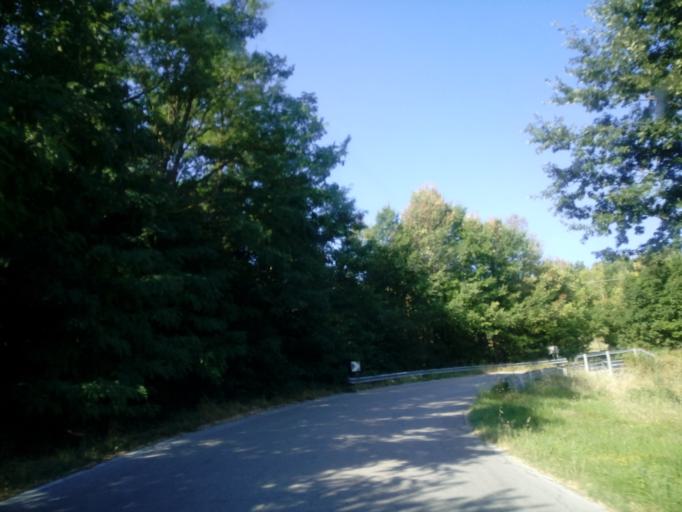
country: IT
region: Molise
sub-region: Provincia di Campobasso
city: Jelsi
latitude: 41.5121
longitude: 14.7724
